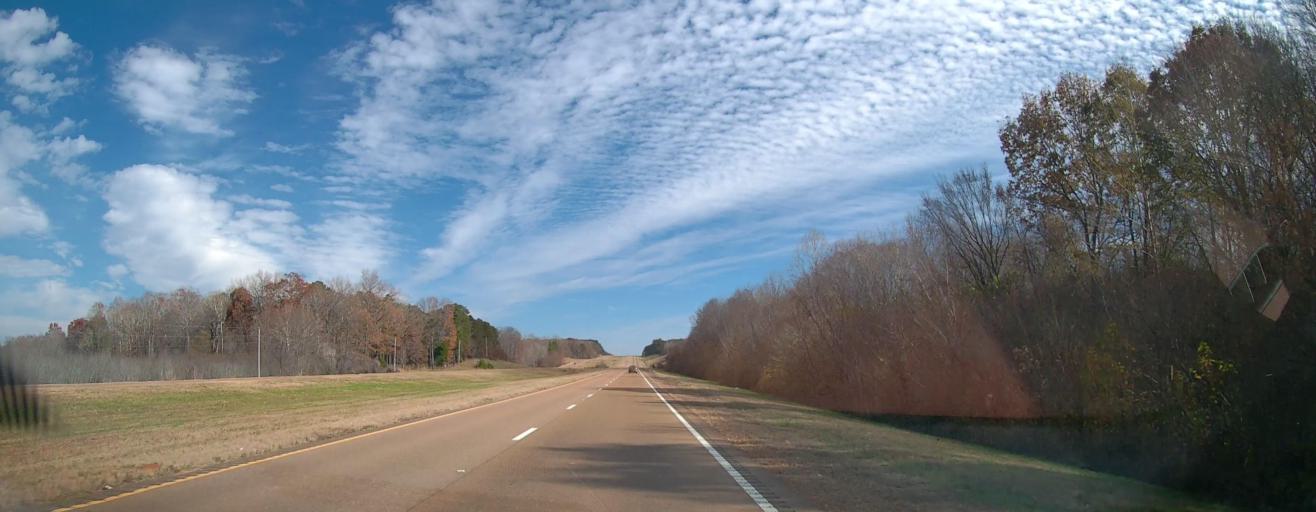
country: US
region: Mississippi
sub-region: Benton County
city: Ashland
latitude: 34.9522
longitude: -89.0573
